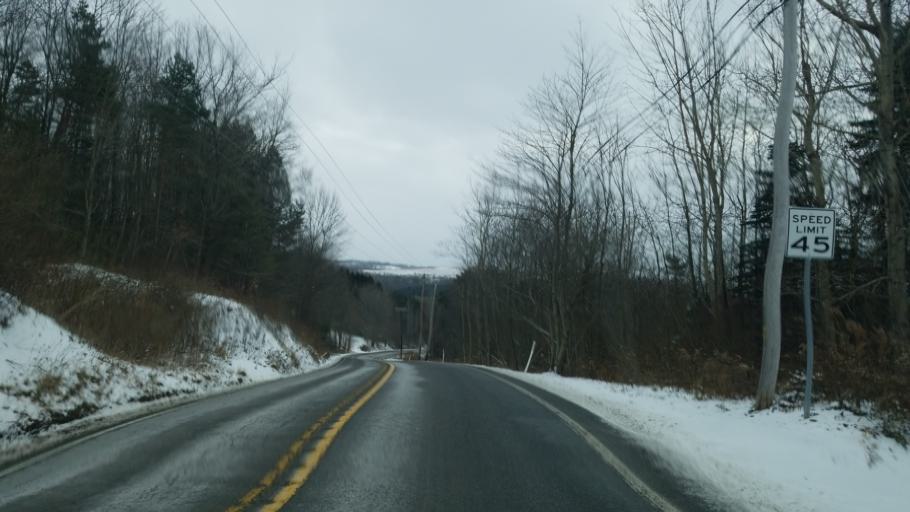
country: US
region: Pennsylvania
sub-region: Clearfield County
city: Sandy
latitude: 41.0839
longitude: -78.7362
